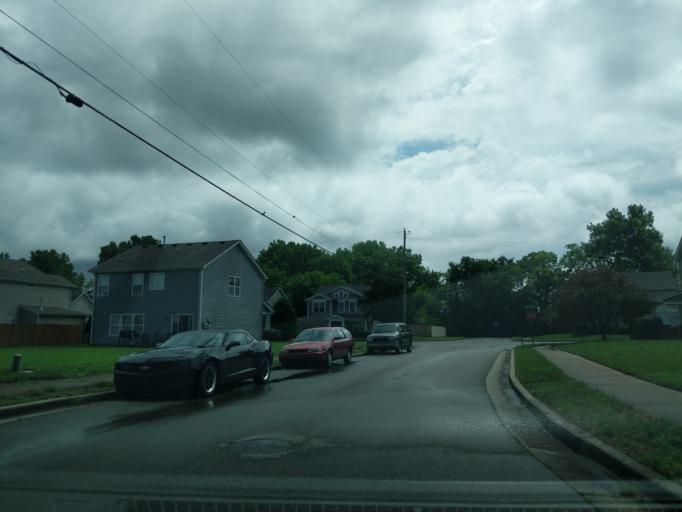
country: US
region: Tennessee
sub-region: Davidson County
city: Lakewood
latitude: 36.2346
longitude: -86.6920
